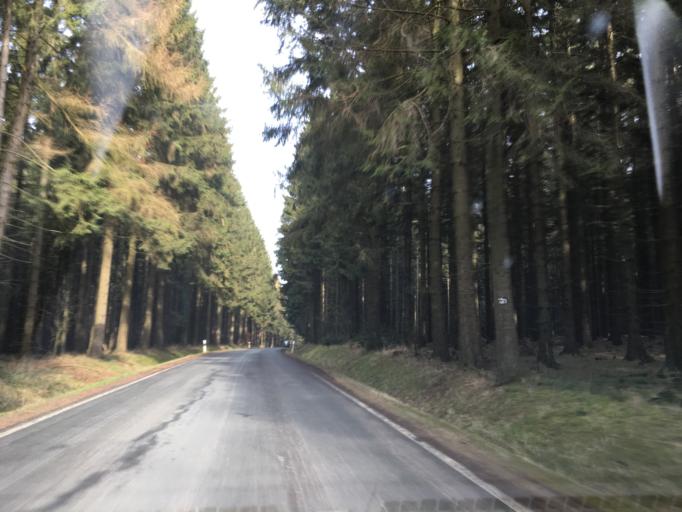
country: DE
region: North Rhine-Westphalia
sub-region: Regierungsbezirk Detmold
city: Willebadessen
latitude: 51.6041
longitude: 8.9919
